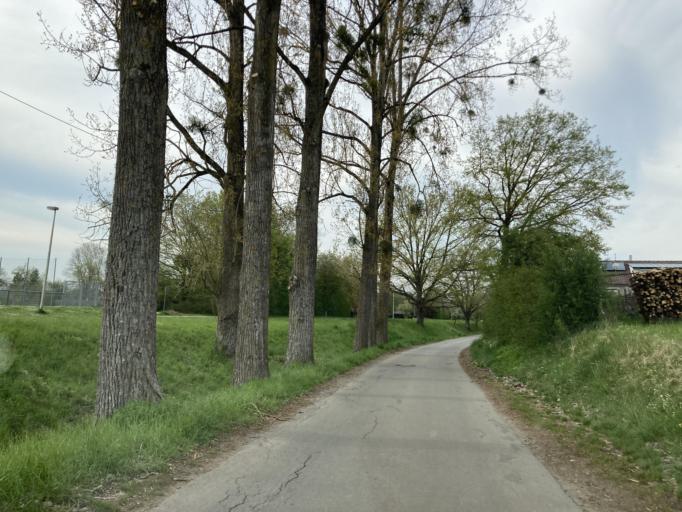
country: DE
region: Baden-Wuerttemberg
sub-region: Tuebingen Region
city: Dusslingen
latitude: 48.4783
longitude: 9.0002
